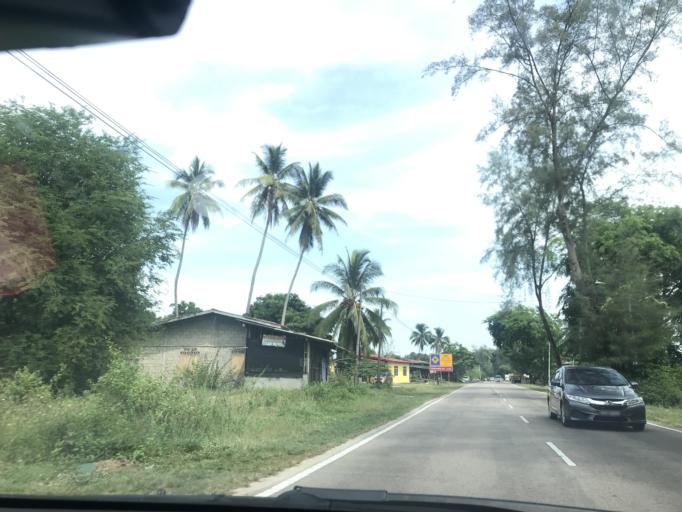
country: MY
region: Kelantan
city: Tumpat
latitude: 6.2087
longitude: 102.1399
